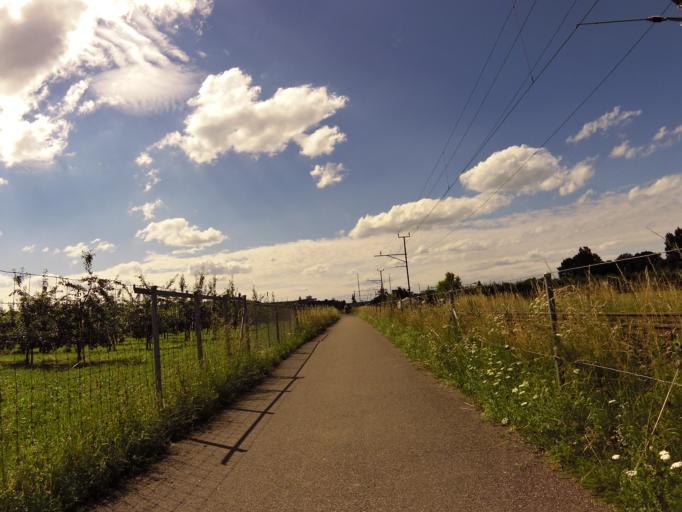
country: CH
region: Thurgau
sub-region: Arbon District
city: Egnach
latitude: 47.5415
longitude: 9.3891
